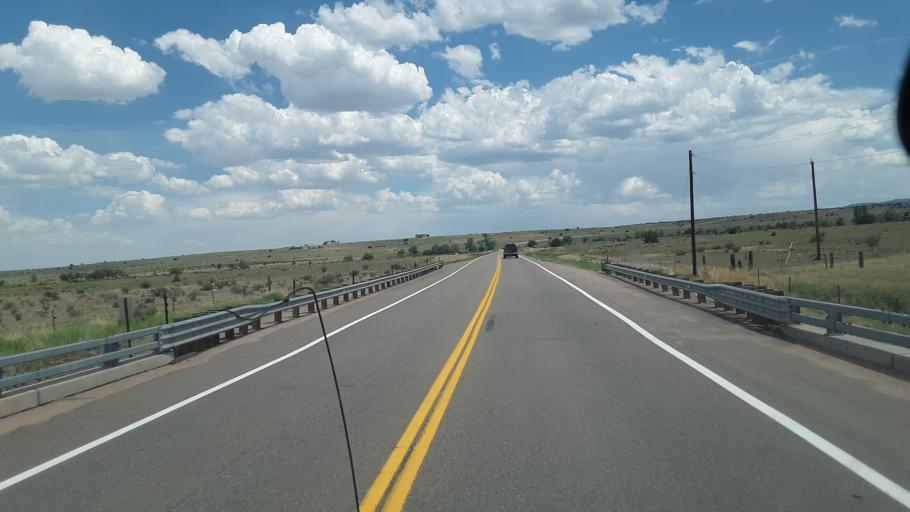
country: US
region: Colorado
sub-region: Fremont County
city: Florence
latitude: 38.3046
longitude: -105.0970
